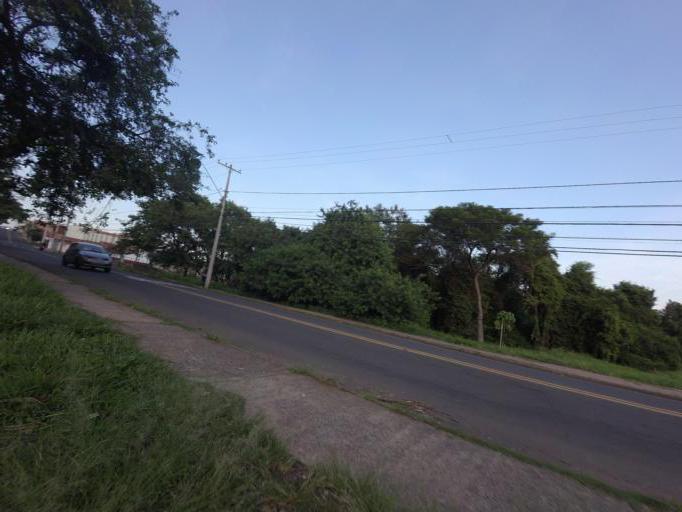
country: BR
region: Sao Paulo
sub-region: Piracicaba
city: Piracicaba
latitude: -22.7574
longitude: -47.6097
